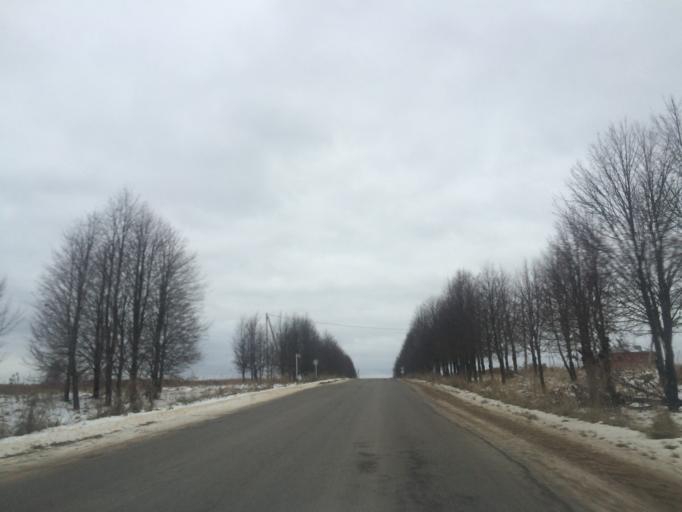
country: RU
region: Tula
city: Kosaya Gora
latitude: 54.1586
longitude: 37.4350
